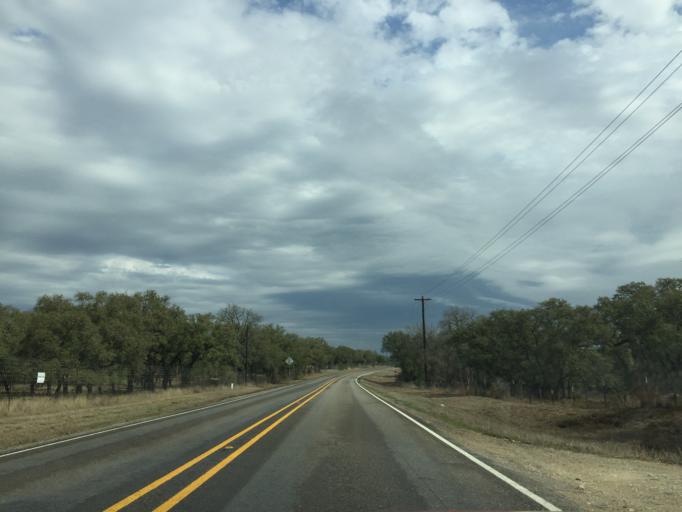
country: US
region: Texas
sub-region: Burnet County
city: Bertram
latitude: 30.6536
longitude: -97.9652
